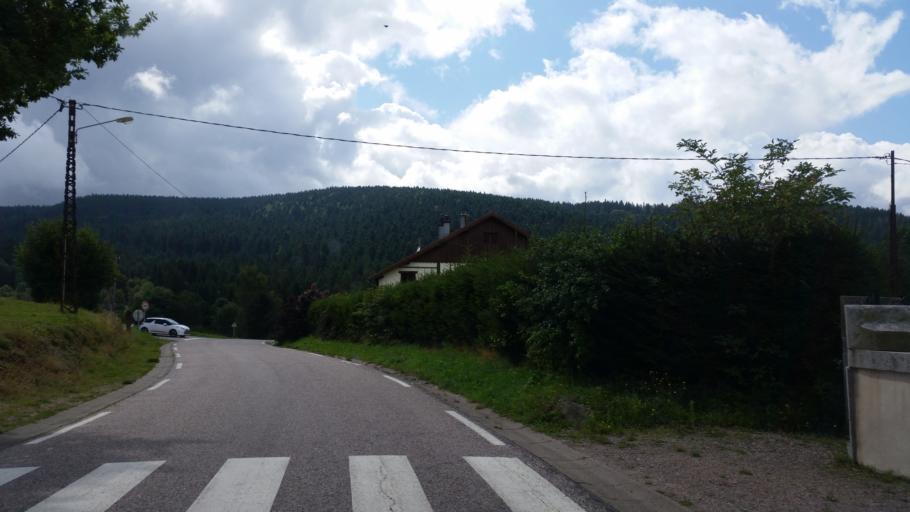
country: FR
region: Lorraine
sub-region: Departement des Vosges
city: Granges-sur-Vologne
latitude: 48.0942
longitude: 6.8051
